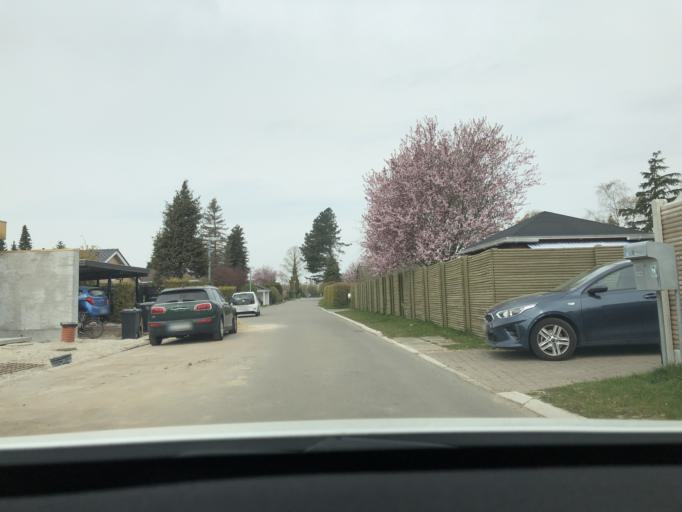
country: DK
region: Zealand
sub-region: Greve Kommune
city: Greve
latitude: 55.5793
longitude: 12.2984
